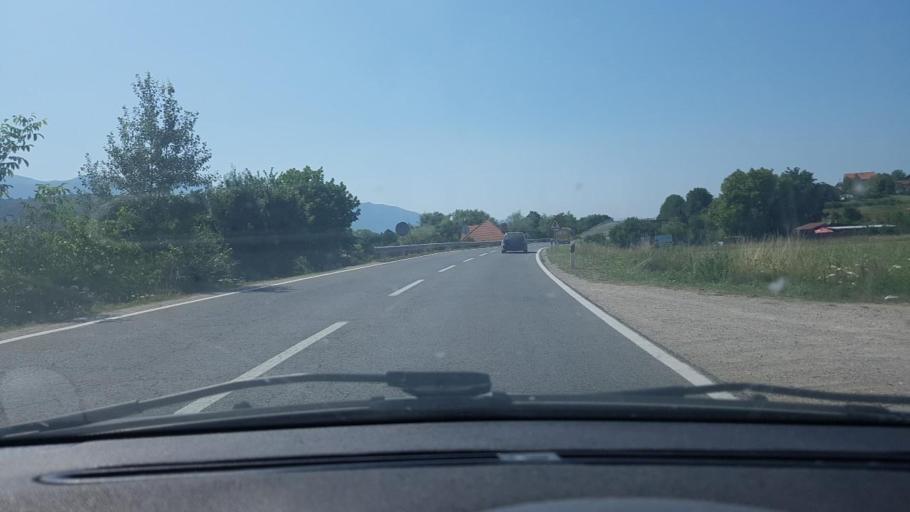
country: BA
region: Federation of Bosnia and Herzegovina
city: Bihac
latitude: 44.7980
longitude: 15.9149
